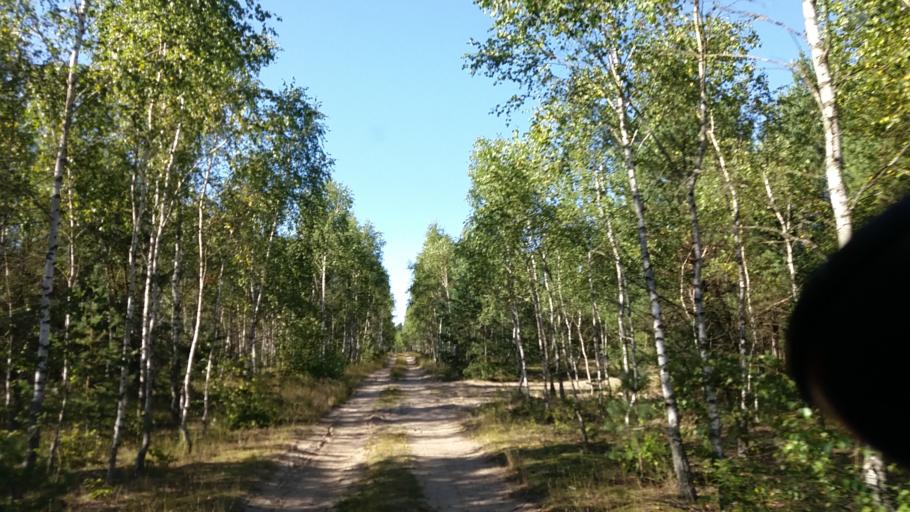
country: PL
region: West Pomeranian Voivodeship
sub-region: Powiat szczecinecki
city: Borne Sulinowo
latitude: 53.5691
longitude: 16.5313
